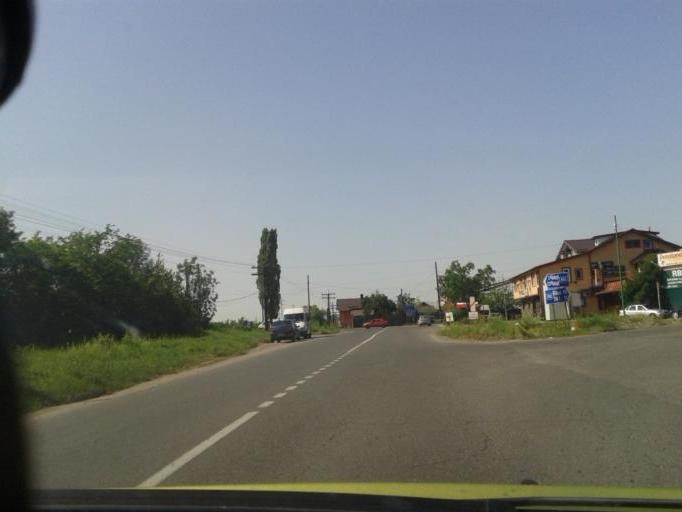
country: RO
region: Prahova
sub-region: Comuna Paulesti
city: Gageni
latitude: 45.0352
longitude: 25.9405
